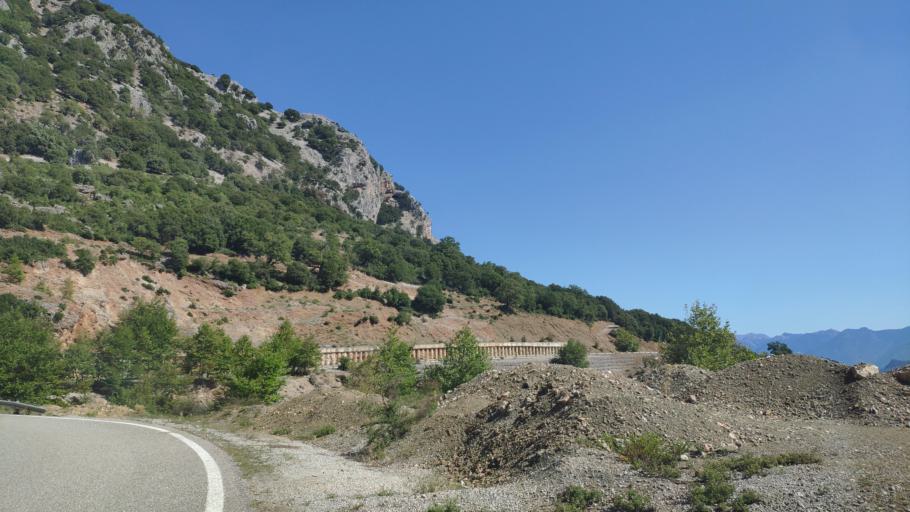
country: GR
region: Central Greece
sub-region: Nomos Evrytanias
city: Kerasochori
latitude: 38.9454
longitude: 21.4593
